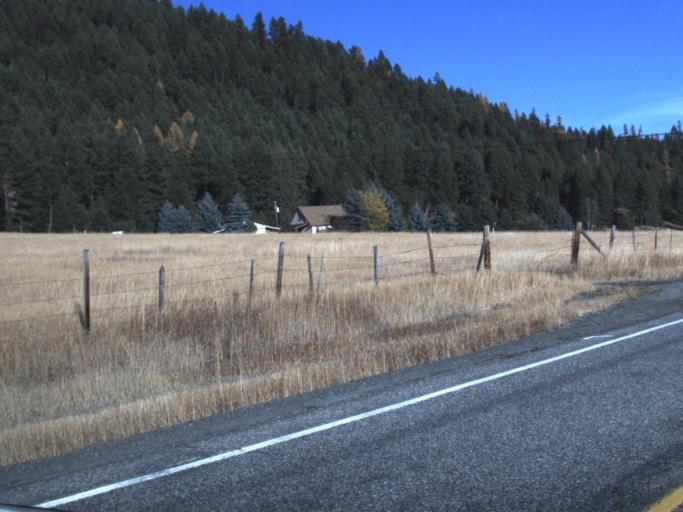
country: US
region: Washington
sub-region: Ferry County
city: Republic
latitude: 48.6119
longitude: -118.7344
